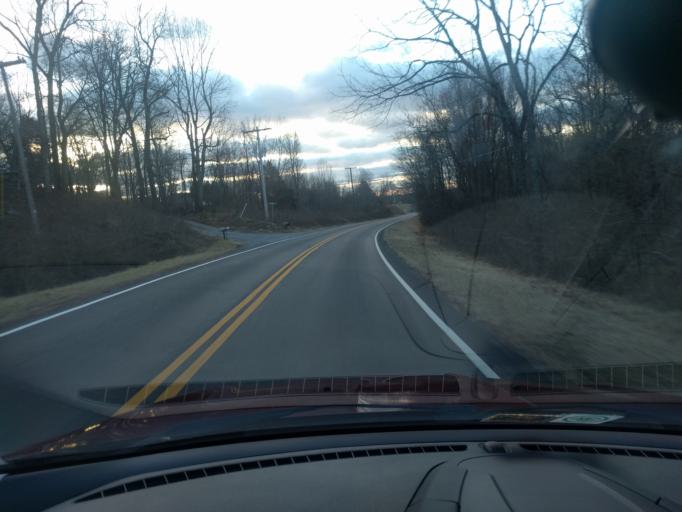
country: US
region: Virginia
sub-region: City of Bedford
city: Bedford
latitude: 37.4204
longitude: -79.5698
